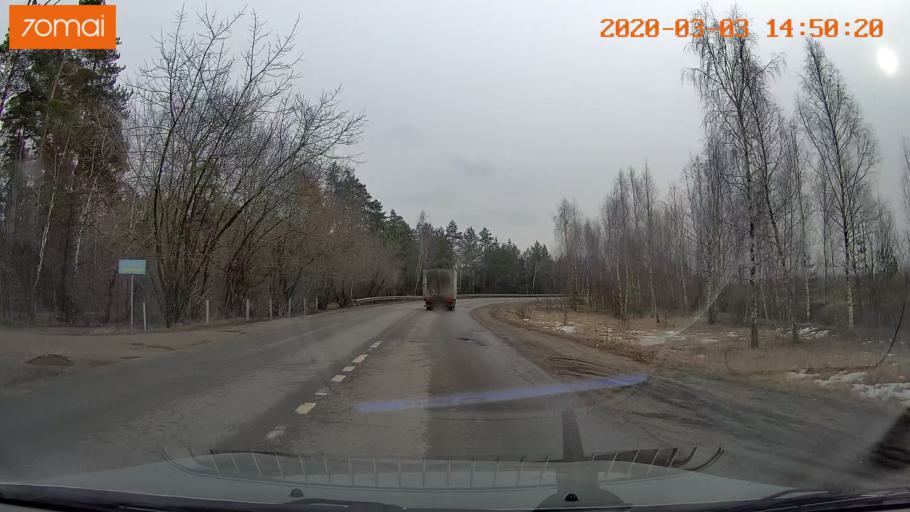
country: RU
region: Moskovskaya
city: Malakhovka
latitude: 55.6716
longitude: 38.0380
